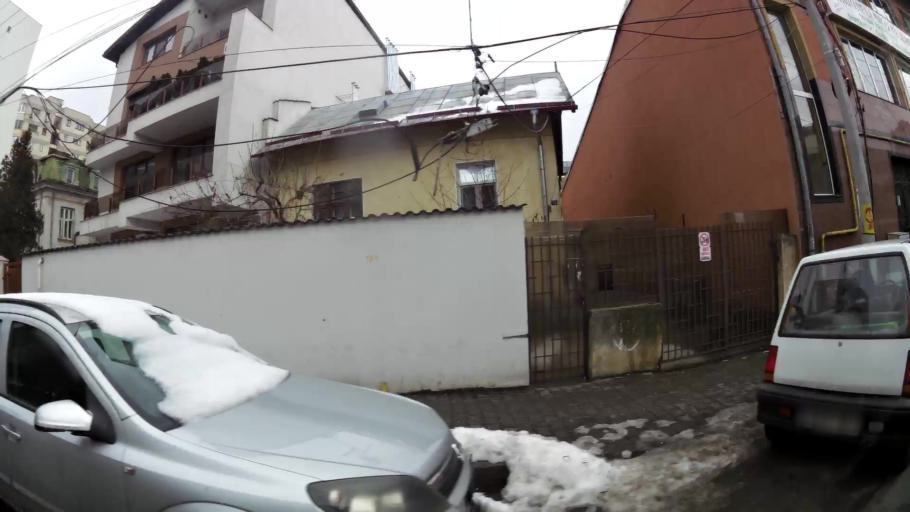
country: RO
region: Bucuresti
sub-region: Municipiul Bucuresti
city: Bucuresti
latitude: 44.4572
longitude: 26.0767
